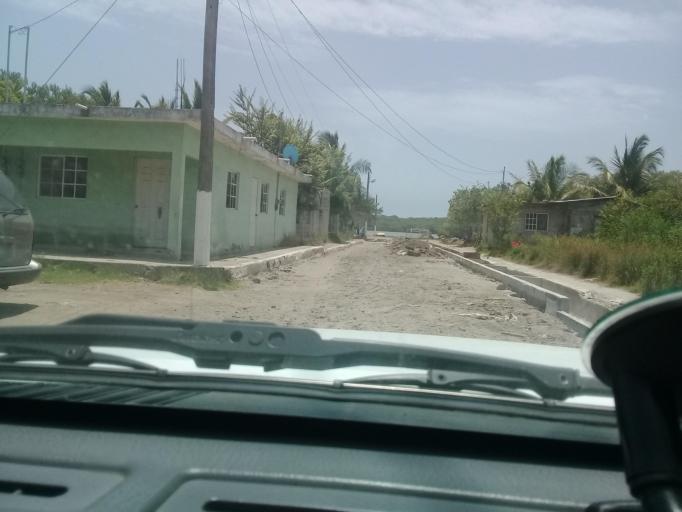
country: MX
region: Veracruz
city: Villa Cuauhtemoc
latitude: 22.2233
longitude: -97.8168
